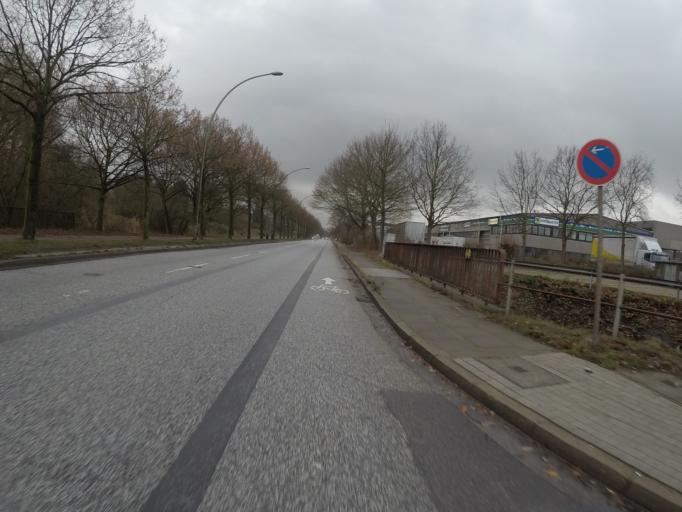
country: DE
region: Hamburg
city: Harburg
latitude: 53.4868
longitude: 9.9905
